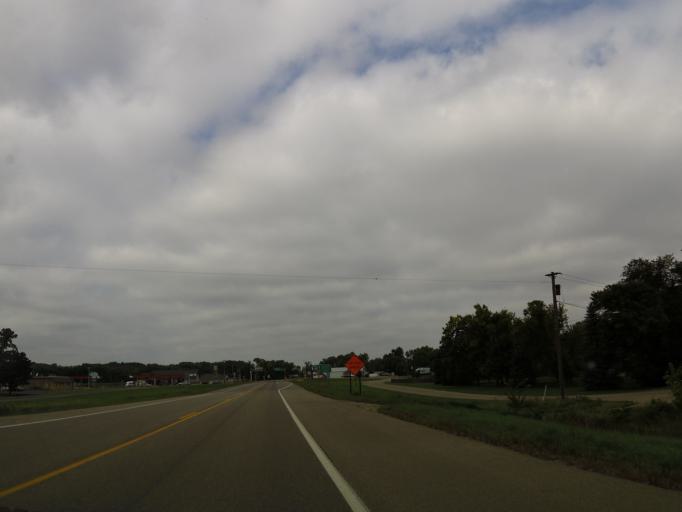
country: US
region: Minnesota
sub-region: Chippewa County
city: Montevideo
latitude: 44.9353
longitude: -95.7249
